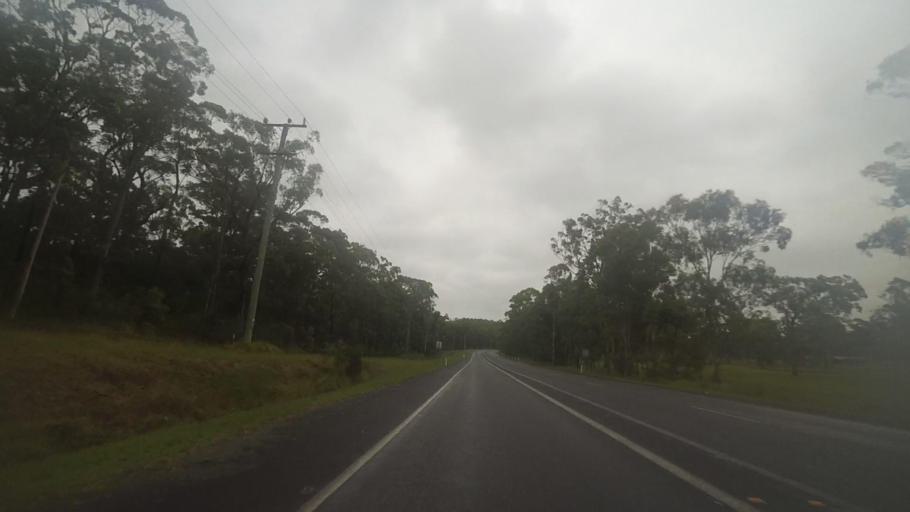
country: AU
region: New South Wales
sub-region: Port Stephens Shire
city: Port Stephens
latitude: -32.6457
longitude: 151.9819
